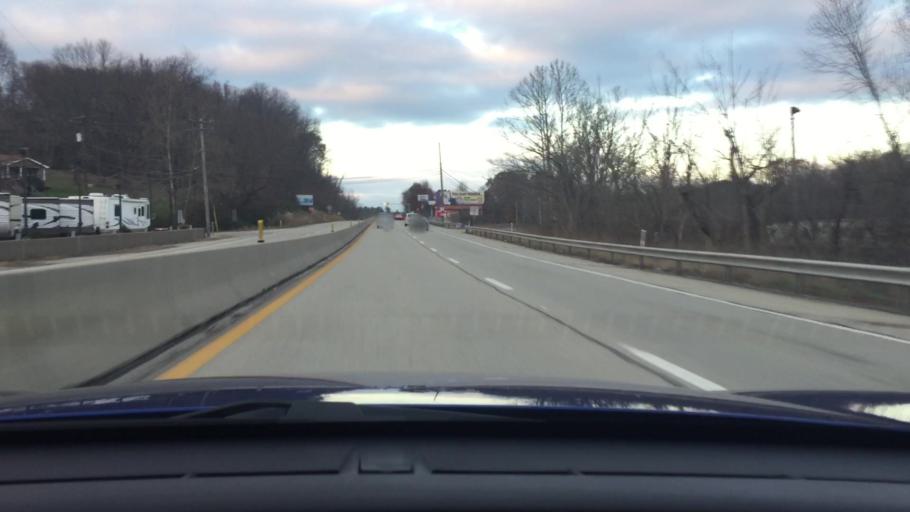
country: US
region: Pennsylvania
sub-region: Westmoreland County
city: Youngwood
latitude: 40.2589
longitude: -79.5688
